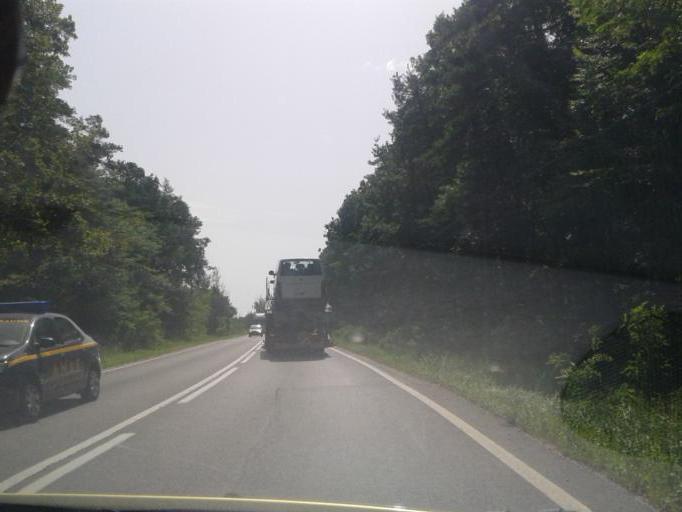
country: RO
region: Arges
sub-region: Comuna Cotmeana
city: Cotmeana
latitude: 44.9899
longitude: 24.6383
